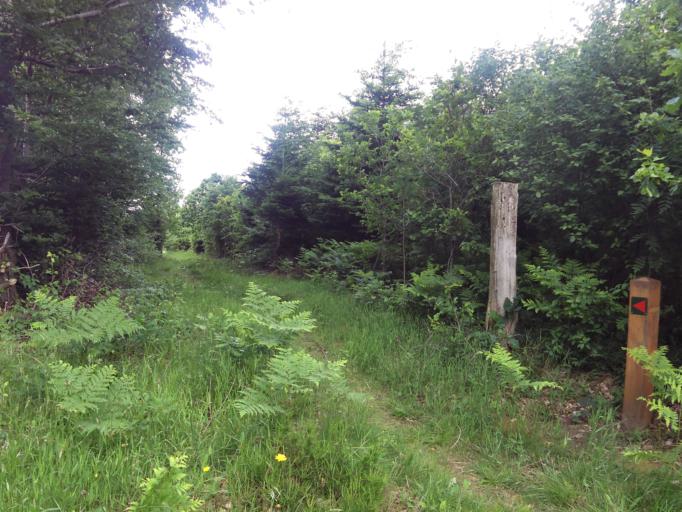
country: DK
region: South Denmark
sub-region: Vejen Kommune
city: Holsted
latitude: 55.4887
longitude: 8.9638
